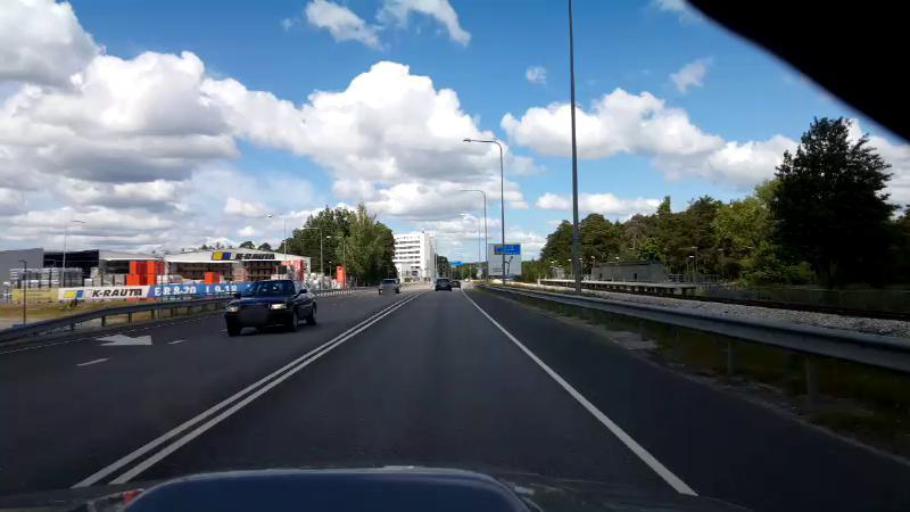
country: EE
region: Paernumaa
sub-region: Paernu linn
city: Parnu
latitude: 58.3734
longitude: 24.5548
